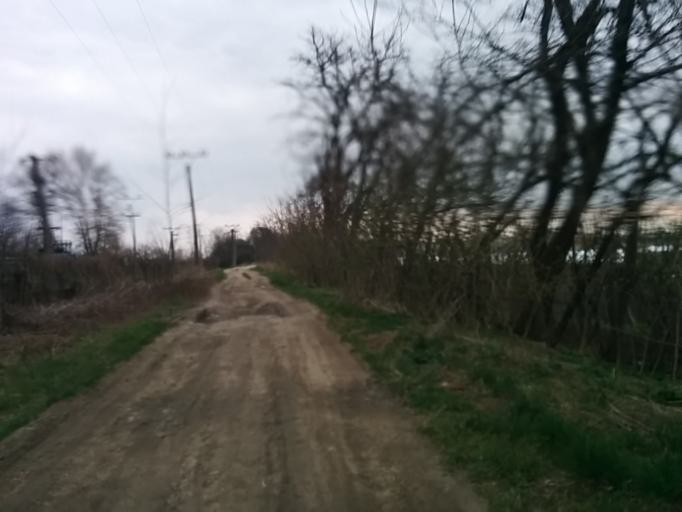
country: SK
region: Nitriansky
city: Sellye
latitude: 48.2380
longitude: 17.8233
